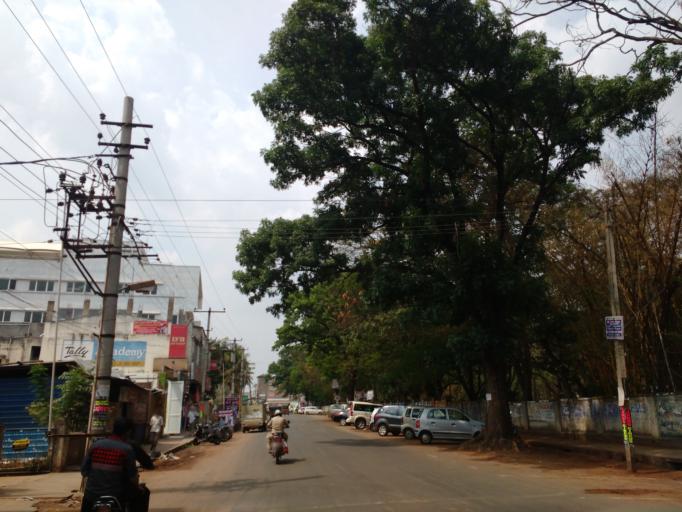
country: IN
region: Karnataka
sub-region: Hassan
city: Hassan
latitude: 13.0080
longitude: 76.1026
